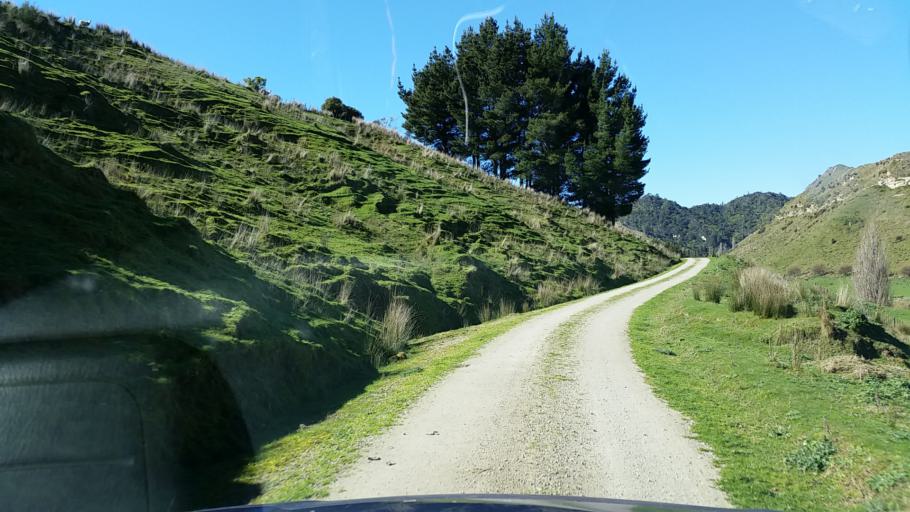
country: NZ
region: Manawatu-Wanganui
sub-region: Wanganui District
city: Wanganui
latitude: -39.6769
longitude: 174.8585
